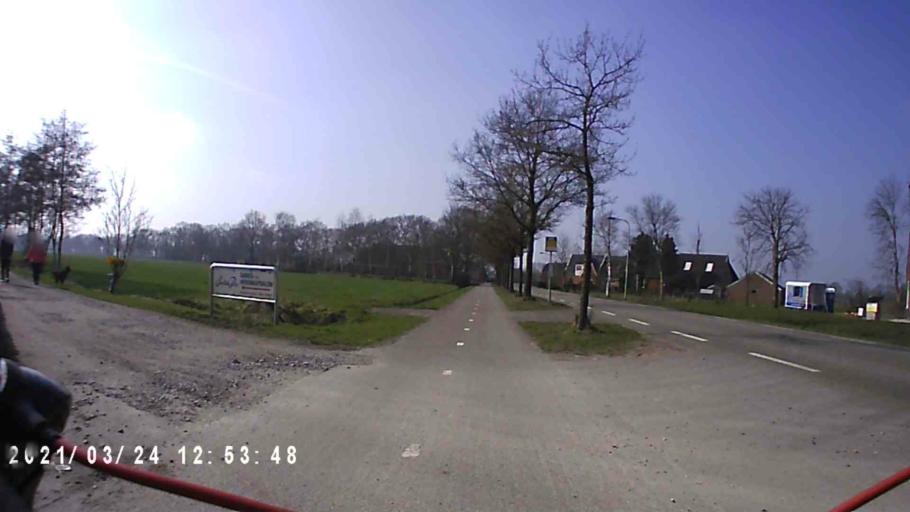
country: NL
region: Groningen
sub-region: Gemeente Leek
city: Leek
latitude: 53.1558
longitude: 6.3177
